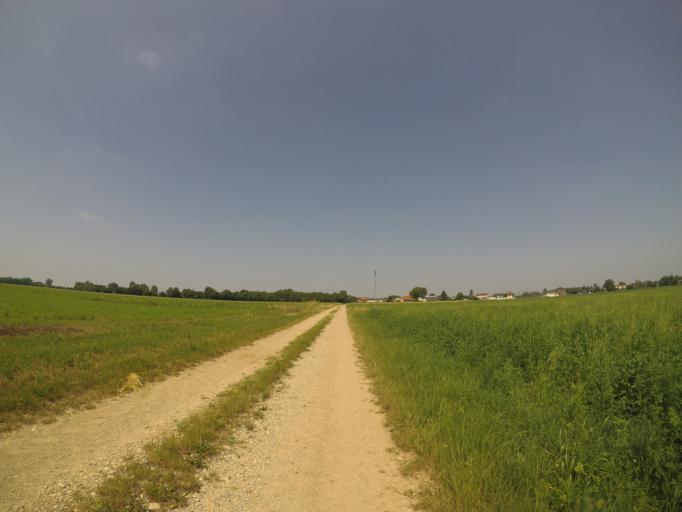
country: IT
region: Friuli Venezia Giulia
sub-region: Provincia di Udine
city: Bertiolo
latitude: 45.9708
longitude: 13.0781
